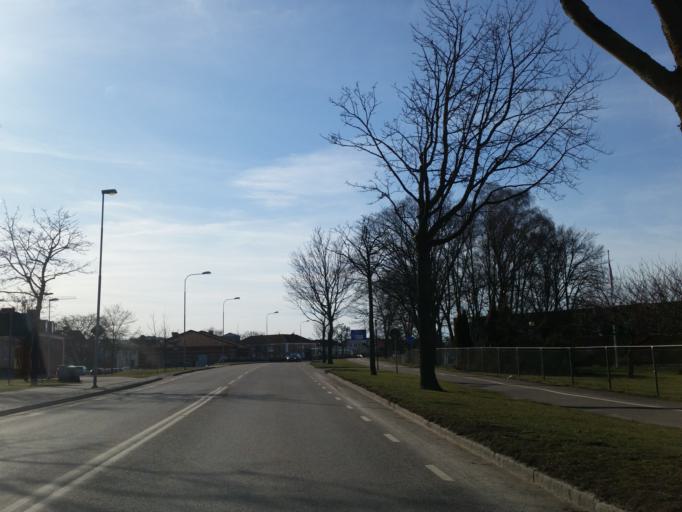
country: SE
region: Kalmar
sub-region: Kalmar Kommun
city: Kalmar
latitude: 56.6631
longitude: 16.3433
